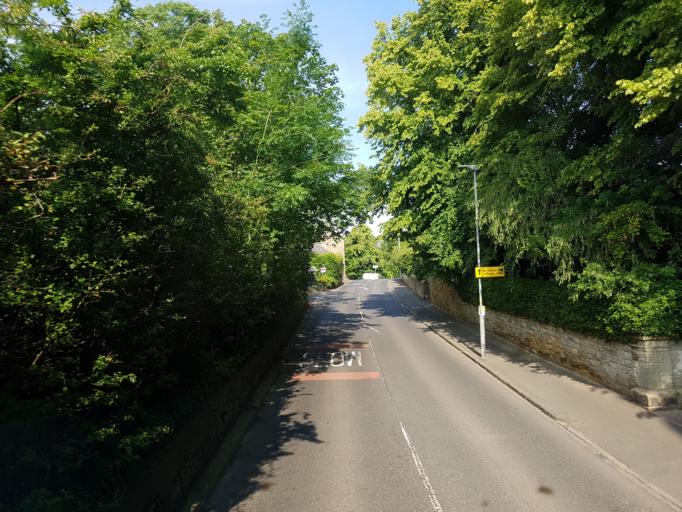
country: GB
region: England
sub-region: Northumberland
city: Alnwick
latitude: 55.4083
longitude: -1.6923
